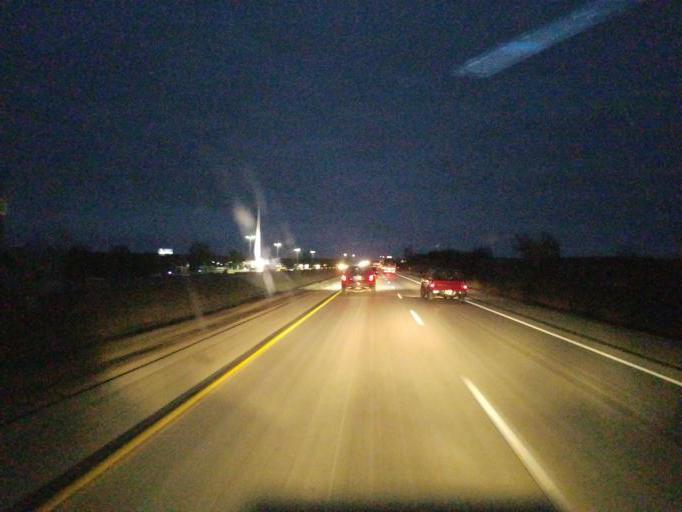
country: US
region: Iowa
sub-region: Guthrie County
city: Guthrie Center
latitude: 41.4967
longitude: -94.5771
